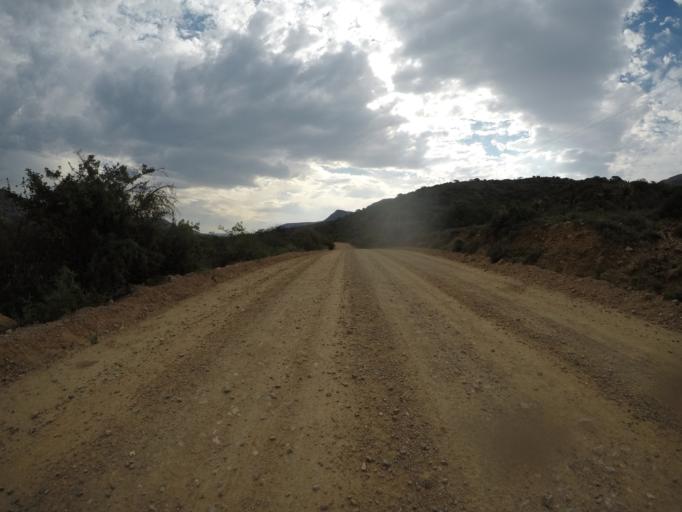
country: ZA
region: Eastern Cape
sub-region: Cacadu District Municipality
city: Kareedouw
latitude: -33.5889
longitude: 24.1730
